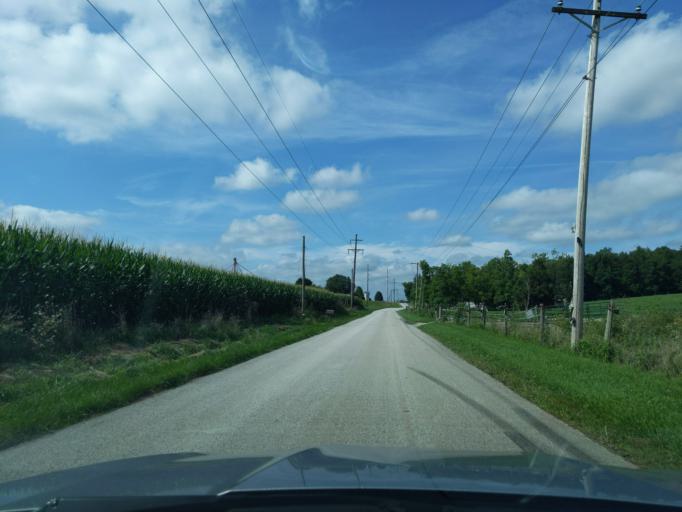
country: US
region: Indiana
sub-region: Ripley County
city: Batesville
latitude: 39.2541
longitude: -85.3475
